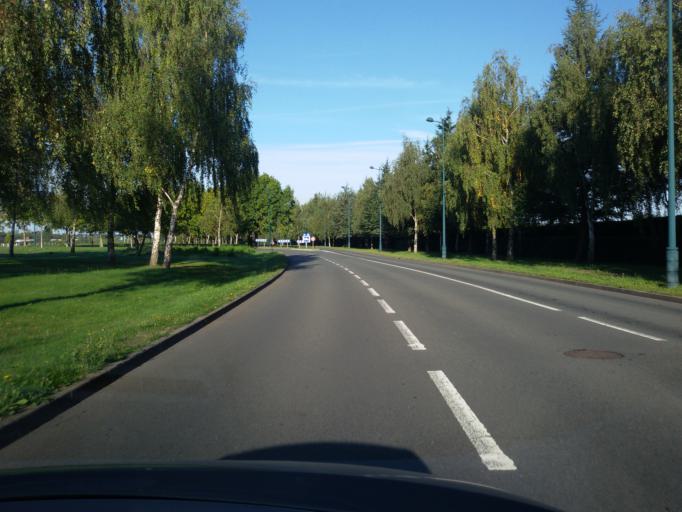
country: FR
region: Ile-de-France
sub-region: Departement de Seine-et-Marne
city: Coupvray
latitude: 48.8786
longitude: 2.7915
